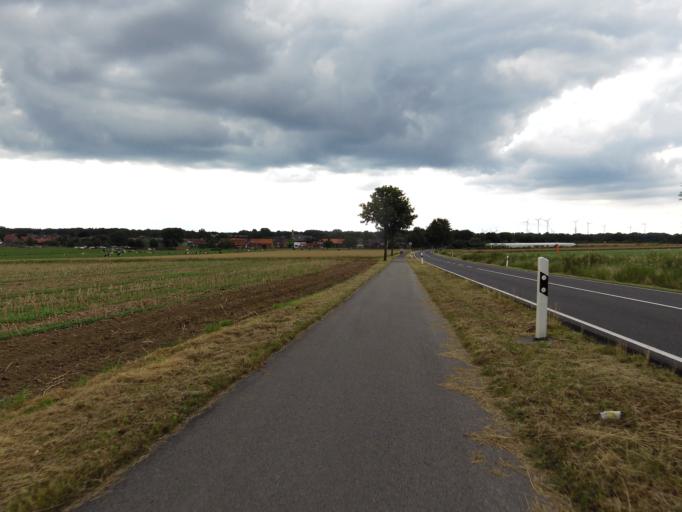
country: DE
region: North Rhine-Westphalia
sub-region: Regierungsbezirk Koln
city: Selfkant
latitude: 51.0153
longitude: 5.9357
